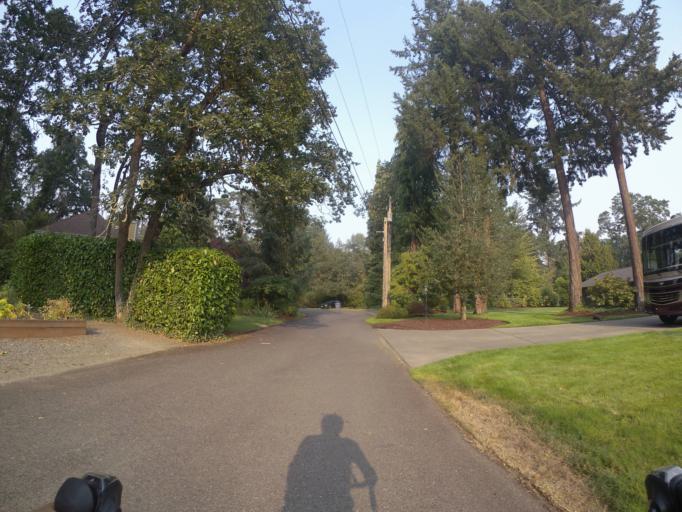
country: US
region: Washington
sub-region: Pierce County
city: Lakewood
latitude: 47.1487
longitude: -122.5214
